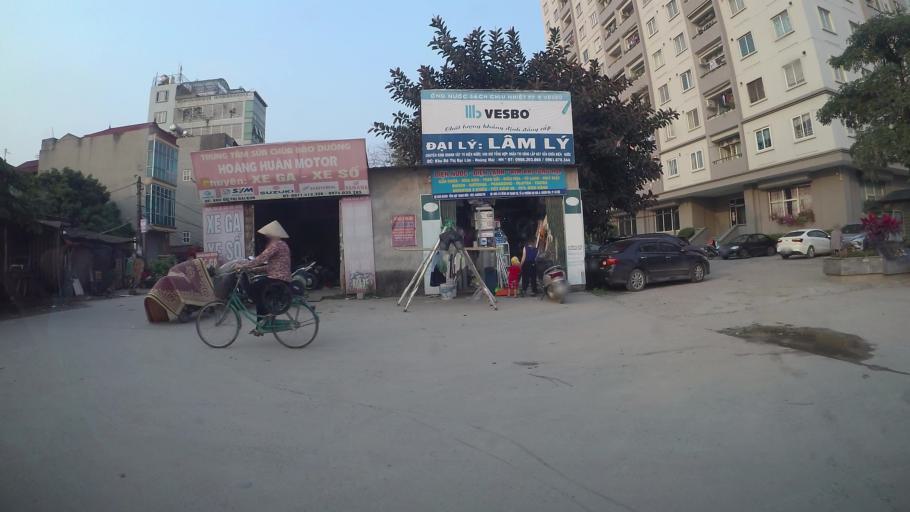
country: VN
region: Ha Noi
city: Thanh Xuan
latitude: 20.9806
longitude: 105.8135
